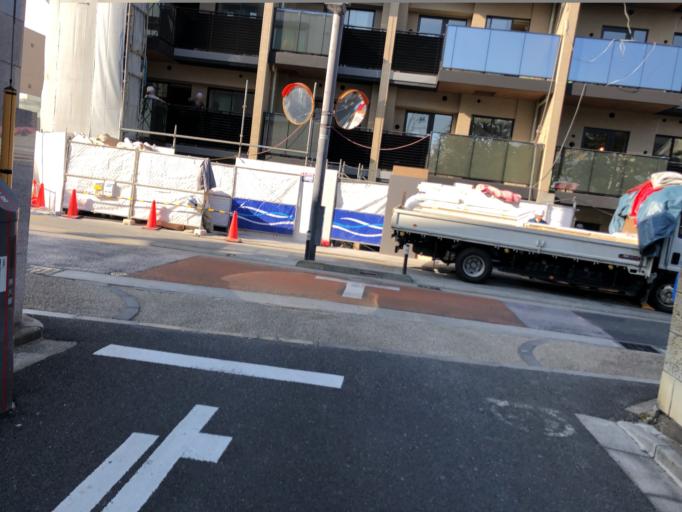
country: JP
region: Tokyo
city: Tokyo
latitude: 35.7264
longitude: 139.7609
